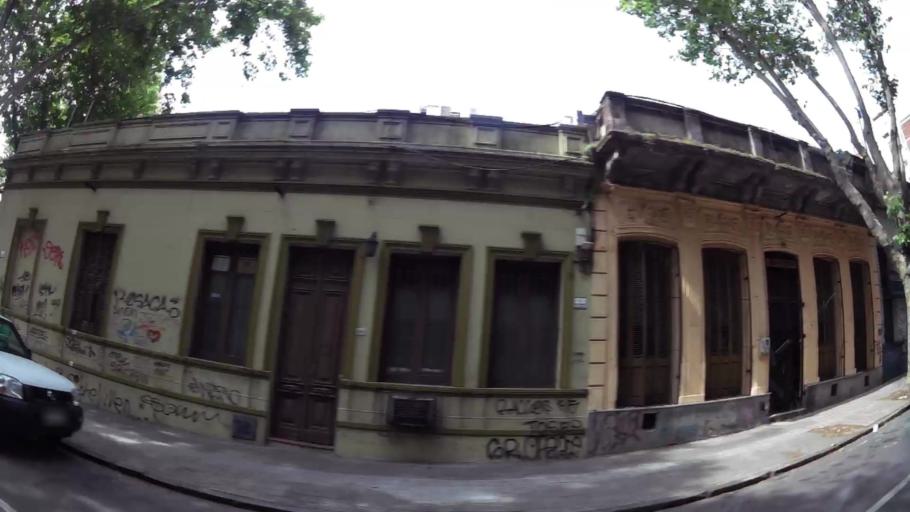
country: UY
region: Montevideo
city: Montevideo
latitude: -34.9081
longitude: -56.1688
